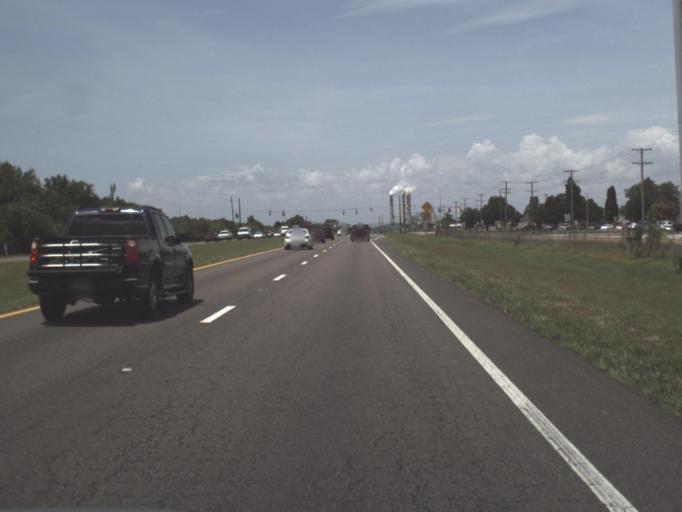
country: US
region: Florida
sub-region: Hillsborough County
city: Apollo Beach
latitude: 27.7920
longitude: -82.3613
